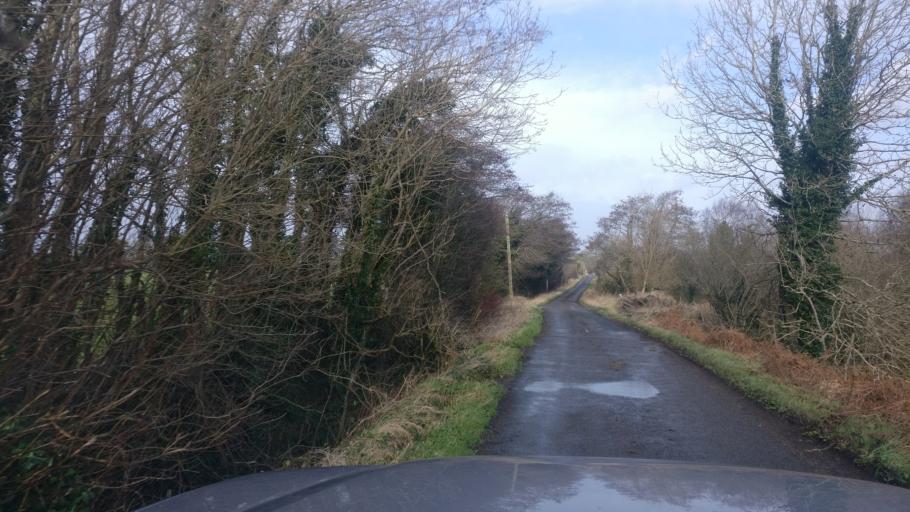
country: IE
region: Connaught
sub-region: County Galway
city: Loughrea
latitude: 53.2741
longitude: -8.5788
